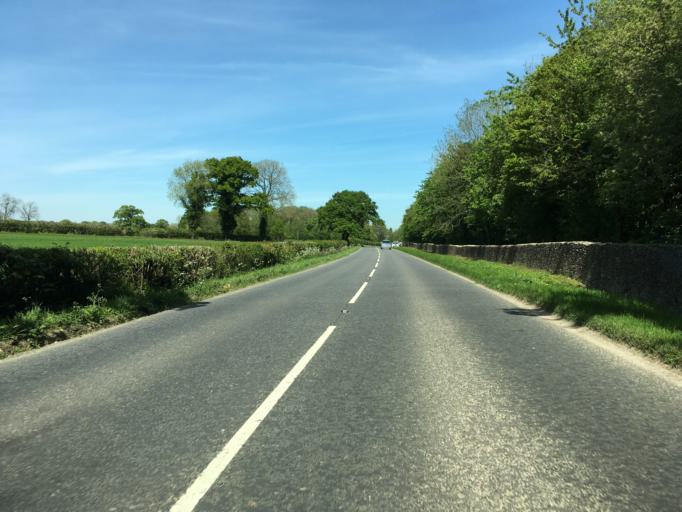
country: GB
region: England
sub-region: Wiltshire
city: Charlton
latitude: 51.6108
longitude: -2.0804
